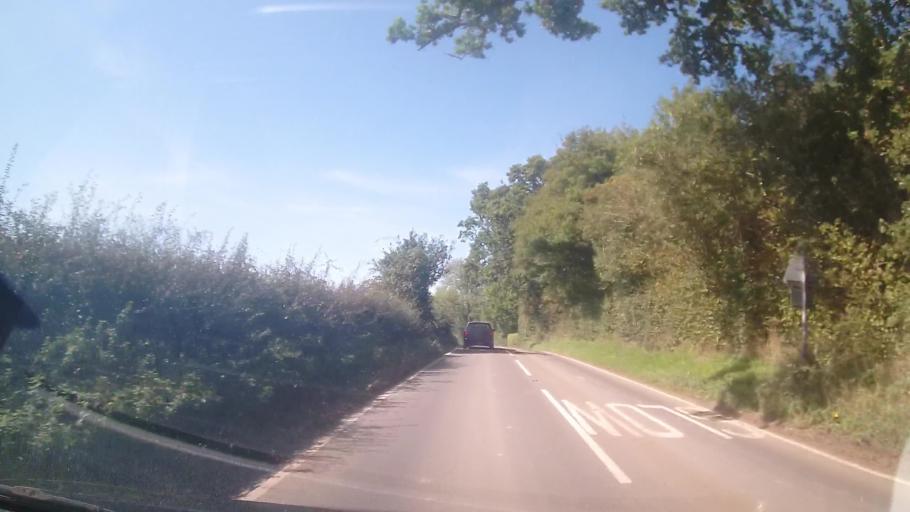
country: GB
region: England
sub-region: Shropshire
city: Lydham
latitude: 52.5207
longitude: -2.9968
